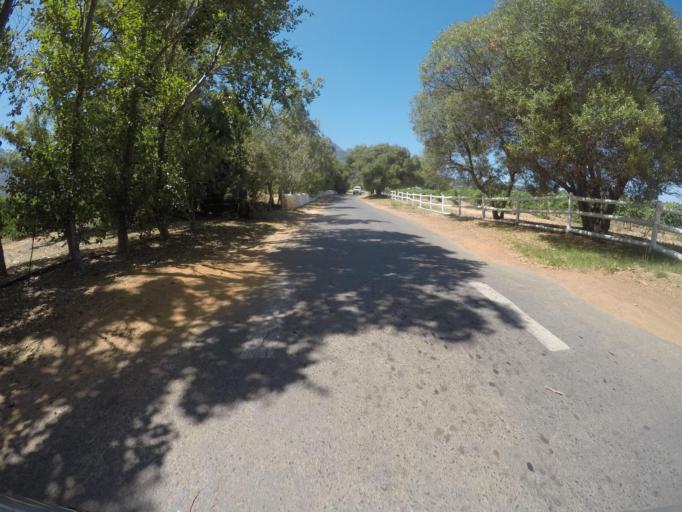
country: ZA
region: Western Cape
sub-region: Cape Winelands District Municipality
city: Stellenbosch
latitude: -33.9917
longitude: 18.8683
